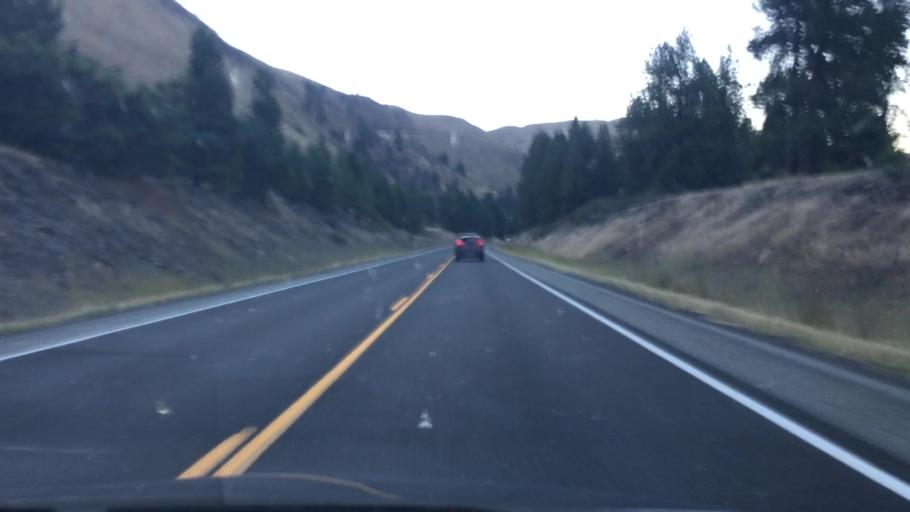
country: US
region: Idaho
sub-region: Valley County
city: McCall
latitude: 45.3004
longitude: -116.3610
